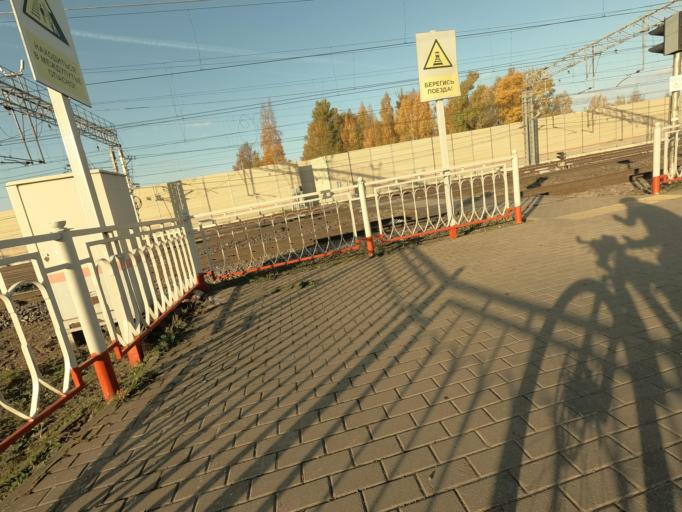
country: RU
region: Leningrad
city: Mga
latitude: 59.7572
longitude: 31.0454
